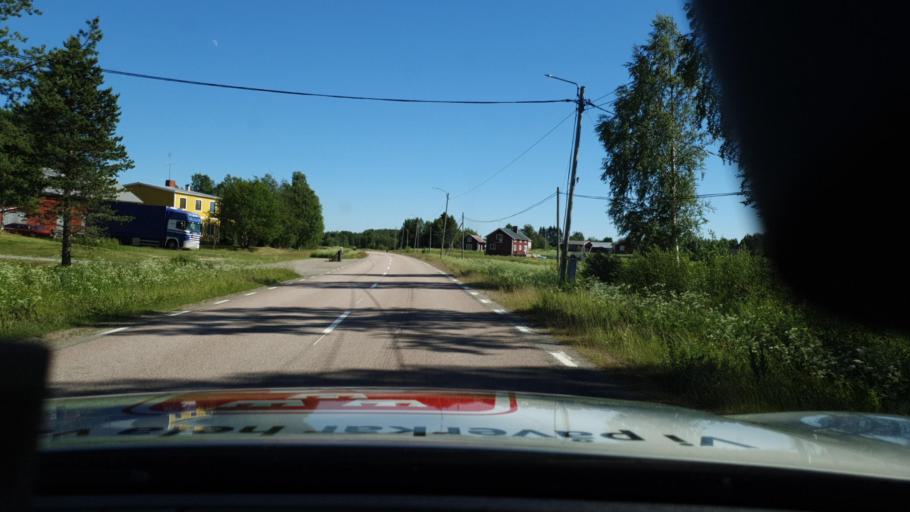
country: SE
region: Norrbotten
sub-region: Lulea Kommun
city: Ranea
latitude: 65.9336
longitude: 22.4139
